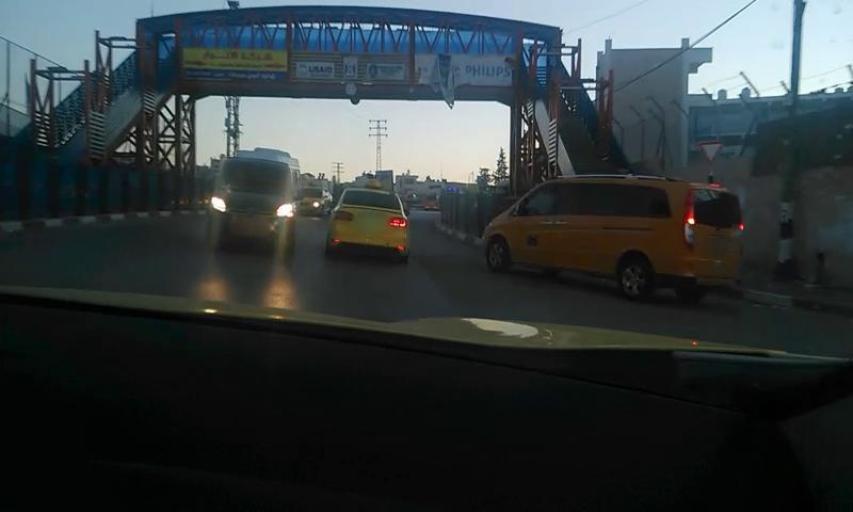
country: PS
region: West Bank
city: Surda
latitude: 31.9450
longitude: 35.2156
